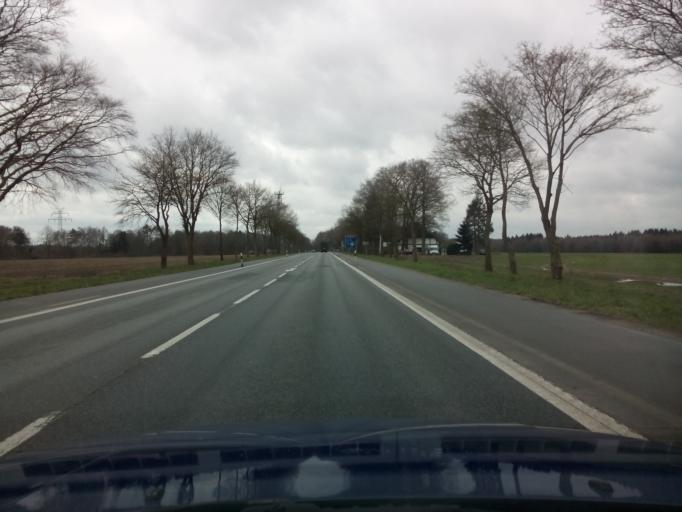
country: DE
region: Lower Saxony
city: Wildeshausen
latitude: 52.9185
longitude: 8.4577
